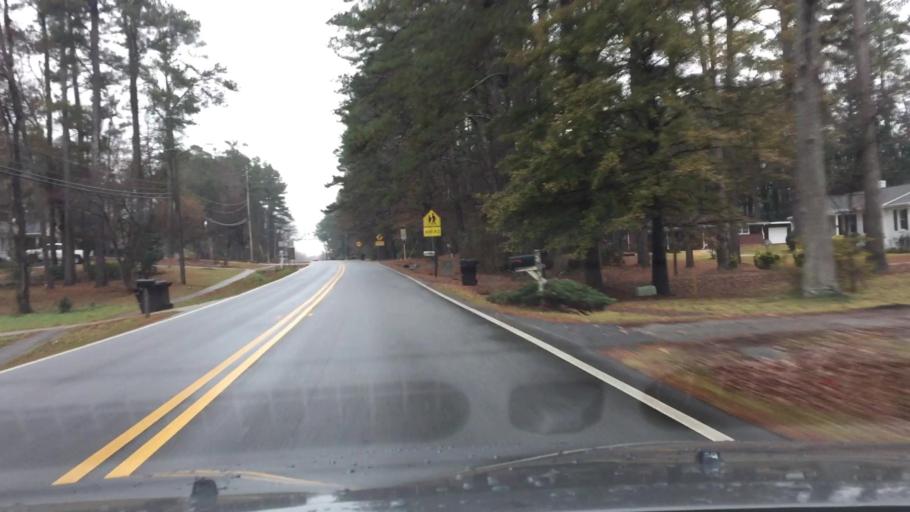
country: US
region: Georgia
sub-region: Cobb County
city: Powder Springs
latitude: 33.8674
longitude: -84.6756
